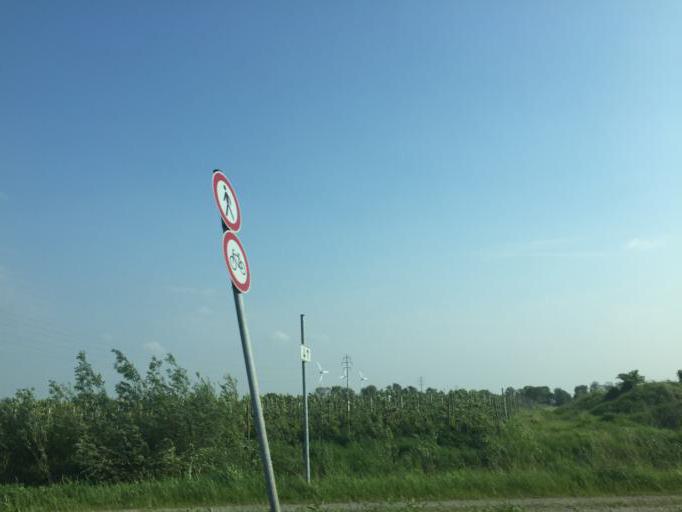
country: DE
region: Hamburg
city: Altona
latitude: 53.5126
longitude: 9.8647
